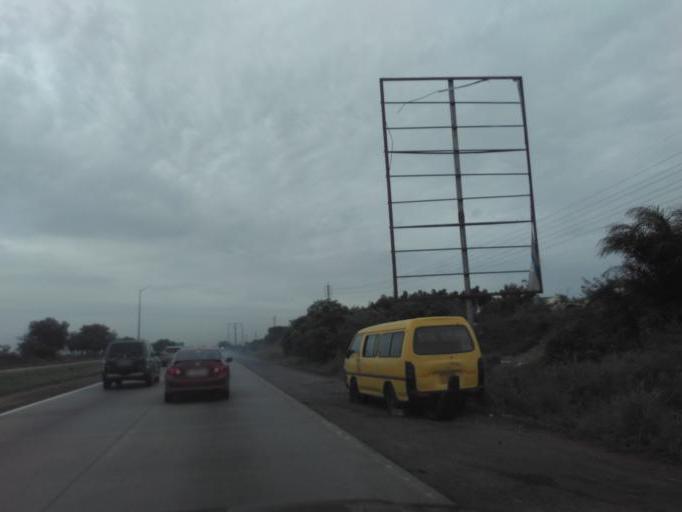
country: GH
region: Greater Accra
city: Tema
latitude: 5.6769
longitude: -0.0388
